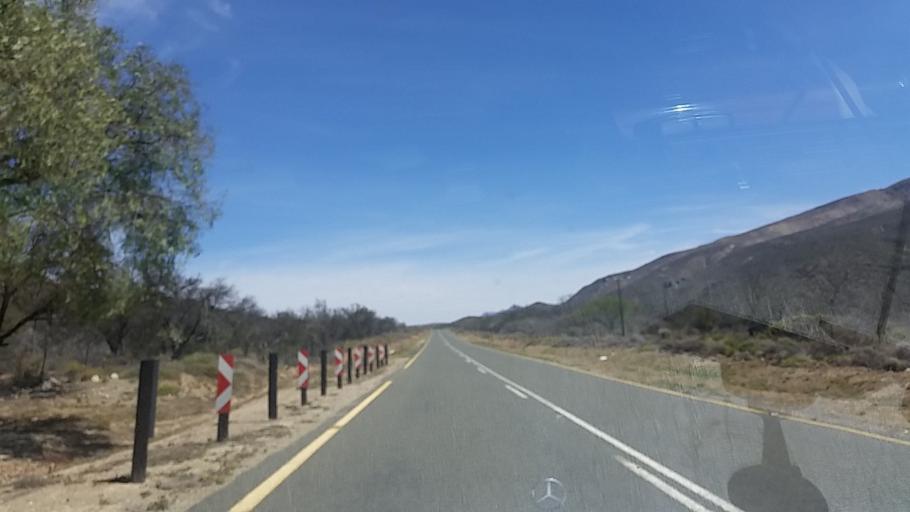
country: ZA
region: Eastern Cape
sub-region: Cacadu District Municipality
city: Willowmore
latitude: -33.4087
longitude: 23.3402
